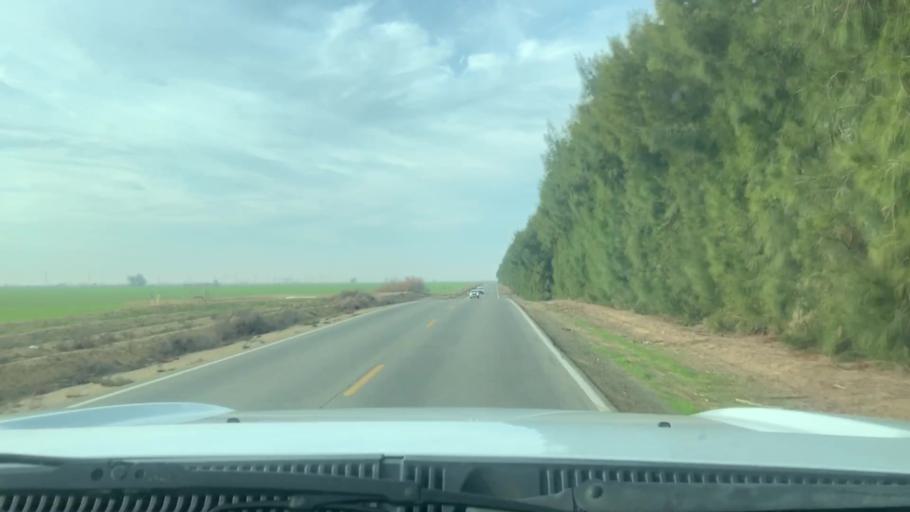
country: US
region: California
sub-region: Kern County
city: Lost Hills
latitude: 35.5054
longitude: -119.7442
